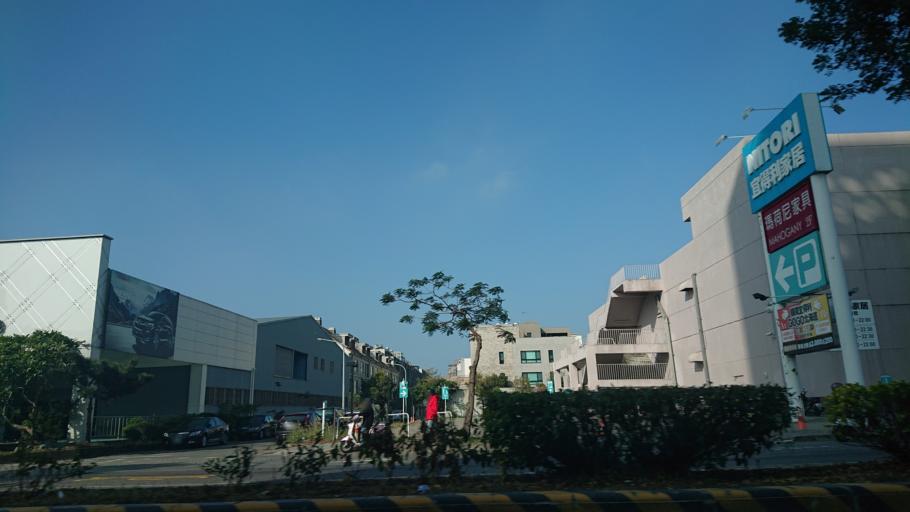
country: TW
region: Taiwan
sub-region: Tainan
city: Tainan
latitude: 23.0019
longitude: 120.1870
